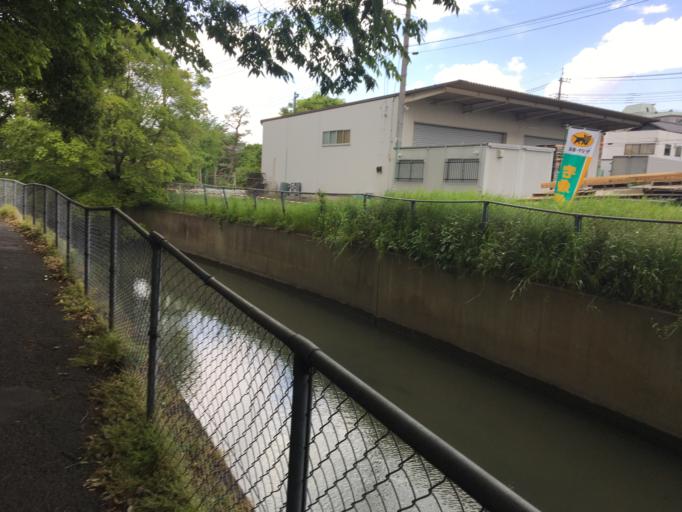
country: JP
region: Saitama
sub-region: Kawaguchi-shi
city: Hatogaya-honcho
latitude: 35.8306
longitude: 139.7502
